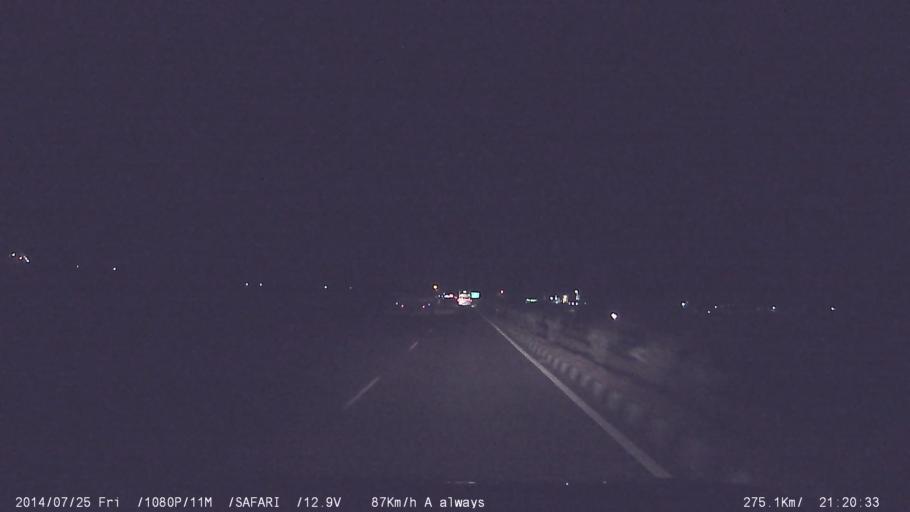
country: IN
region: Tamil Nadu
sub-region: Erode
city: Perundurai
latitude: 11.2916
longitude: 77.5817
